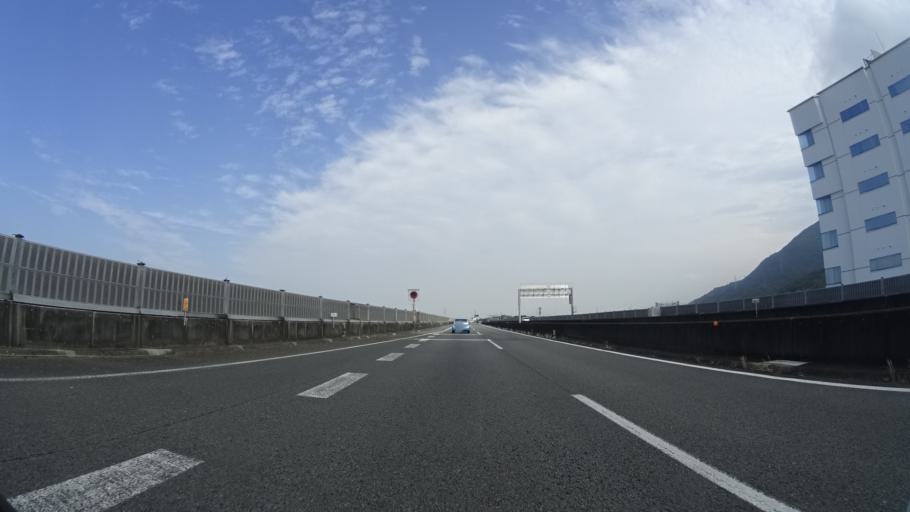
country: JP
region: Kumamoto
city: Yatsushiro
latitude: 32.5061
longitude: 130.6462
